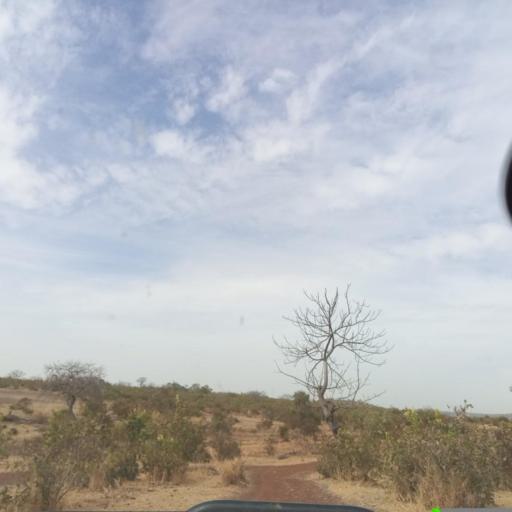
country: ML
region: Koulikoro
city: Koulikoro
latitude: 13.1704
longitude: -7.7311
